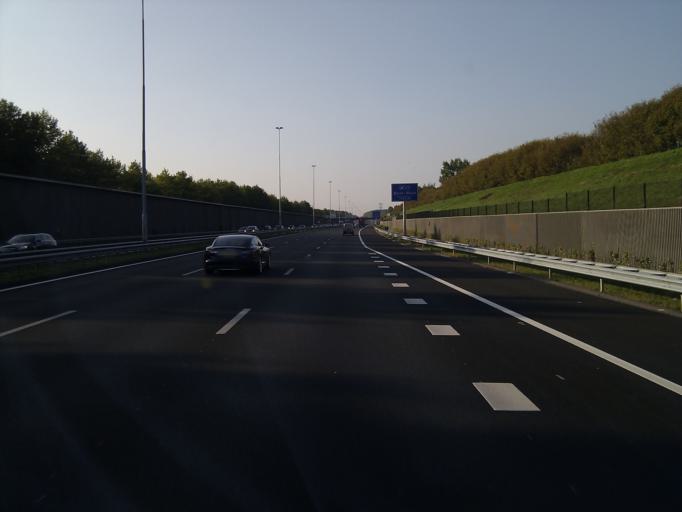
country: NL
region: North Brabant
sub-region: Gemeente Best
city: Best
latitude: 51.5123
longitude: 5.4052
